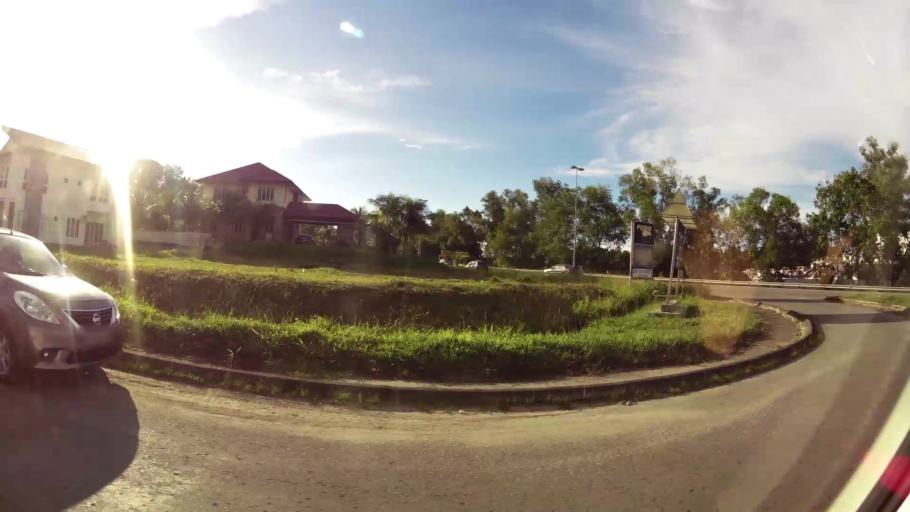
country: BN
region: Brunei and Muara
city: Bandar Seri Begawan
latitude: 4.9772
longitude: 114.9821
